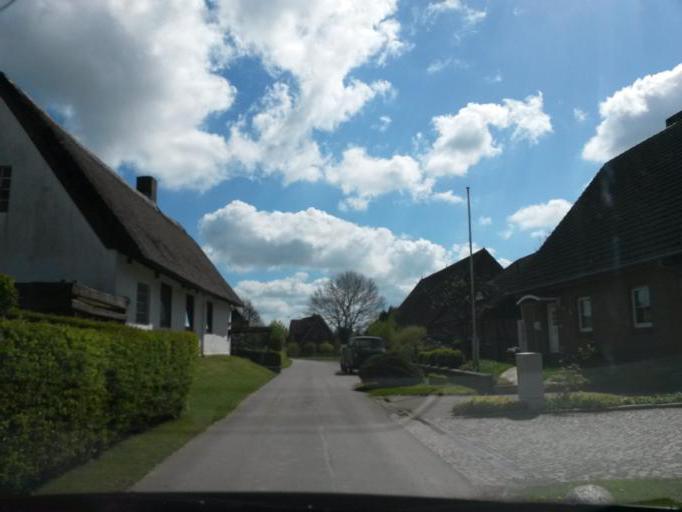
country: DE
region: Schleswig-Holstein
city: Seestermuhe
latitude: 53.6635
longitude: 9.5650
